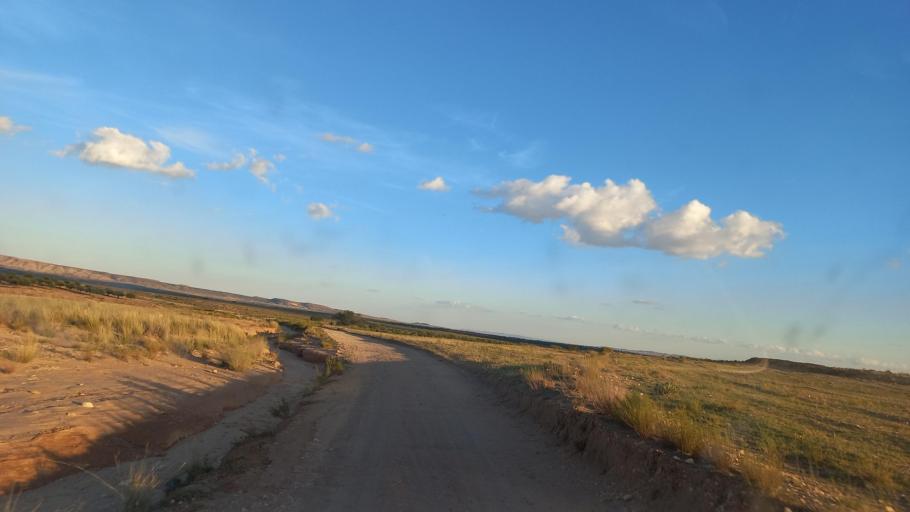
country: TN
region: Al Qasrayn
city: Sbiba
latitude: 35.3491
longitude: 9.0244
